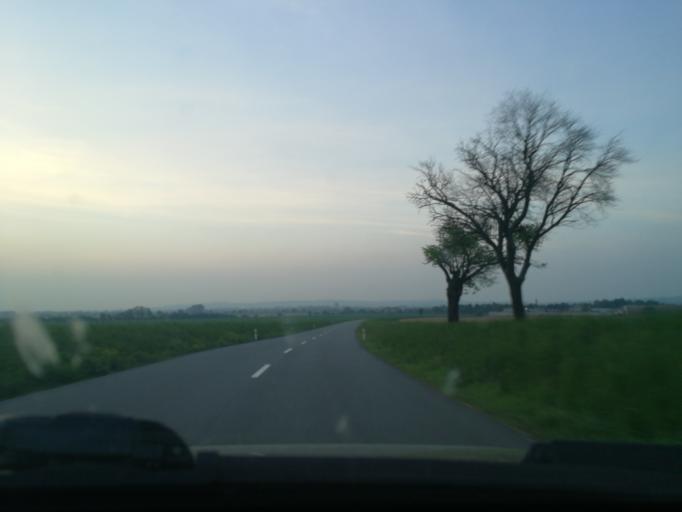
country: CZ
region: Zlin
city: Holesov
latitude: 49.2959
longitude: 17.5573
